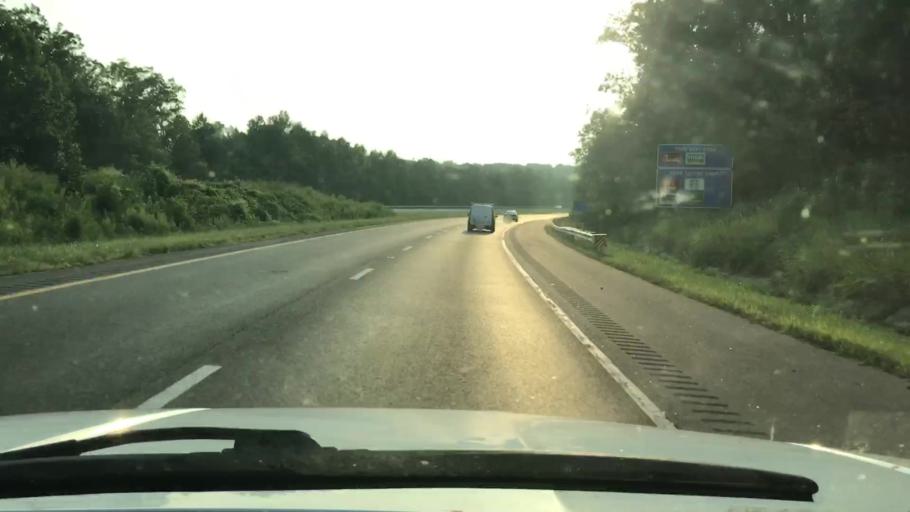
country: US
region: Virginia
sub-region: Chesterfield County
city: Brandermill
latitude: 37.4099
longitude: -77.6101
